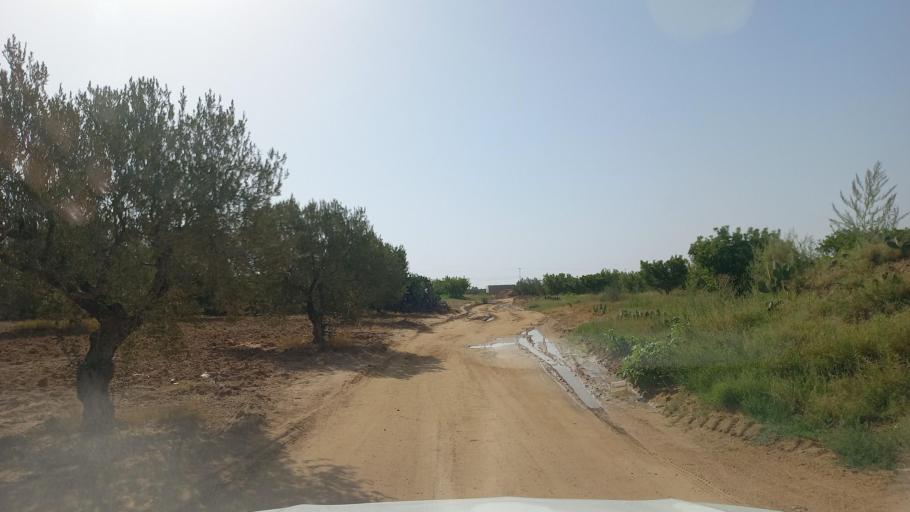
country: TN
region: Al Qasrayn
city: Kasserine
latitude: 35.2424
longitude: 9.0355
